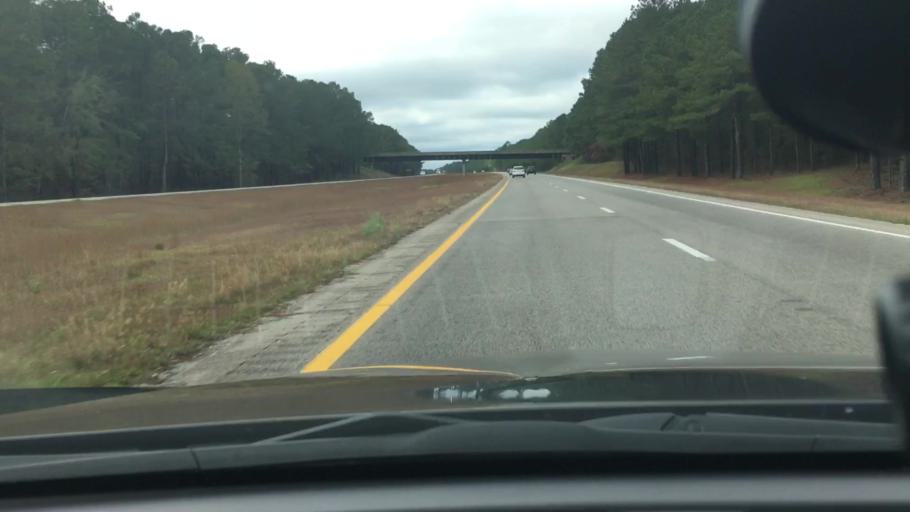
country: US
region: North Carolina
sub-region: Nash County
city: Spring Hope
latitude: 35.7849
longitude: -78.0954
